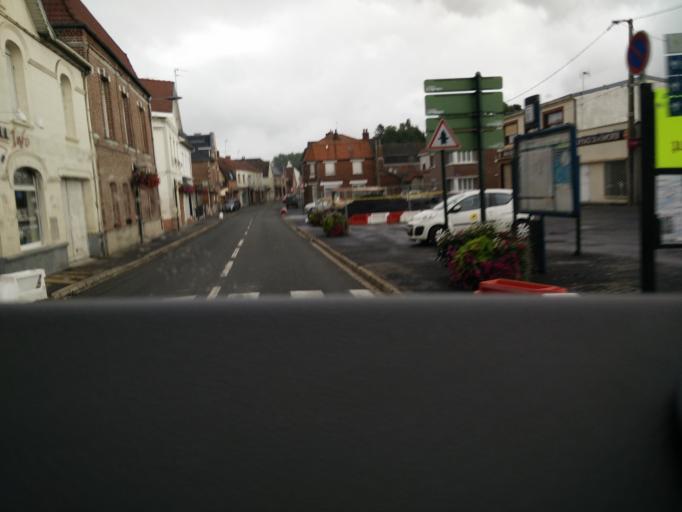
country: FR
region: Nord-Pas-de-Calais
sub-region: Departement du Pas-de-Calais
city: Aubigny-en-Artois
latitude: 50.3515
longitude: 2.5918
